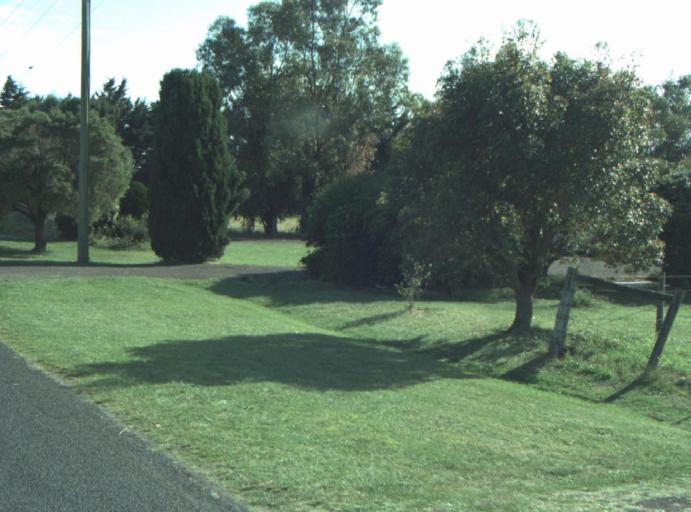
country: AU
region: Victoria
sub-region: Greater Geelong
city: Leopold
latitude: -38.1805
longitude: 144.4381
